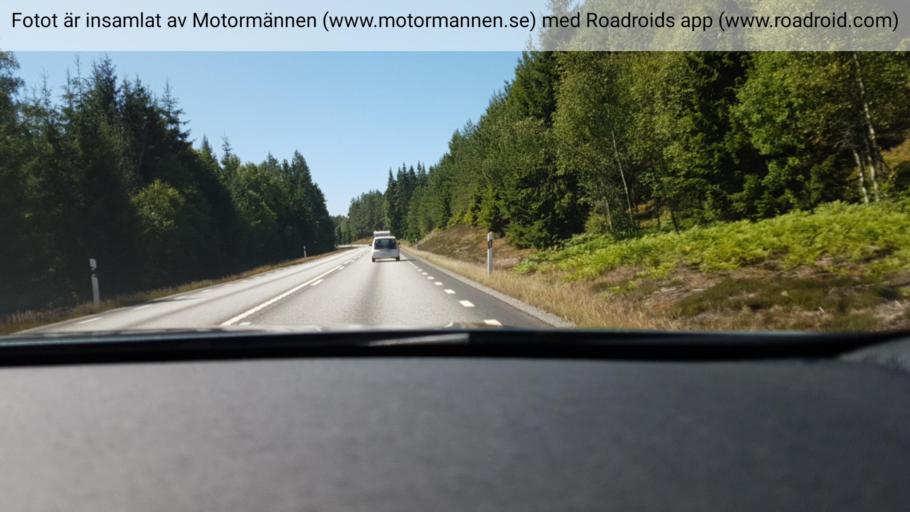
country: SE
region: Joenkoeping
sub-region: Gnosjo Kommun
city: Gnosjoe
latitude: 57.5172
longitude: 13.6803
